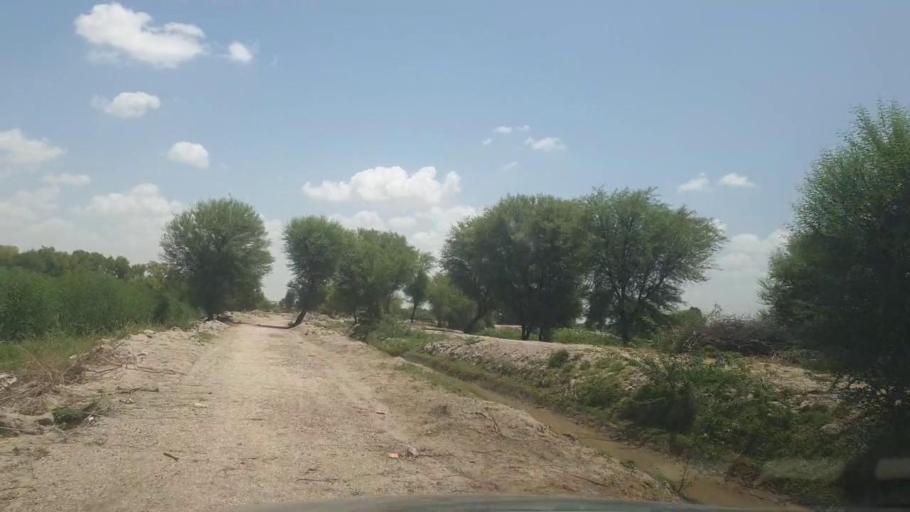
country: PK
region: Sindh
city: Kot Diji
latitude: 27.2570
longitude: 69.0495
